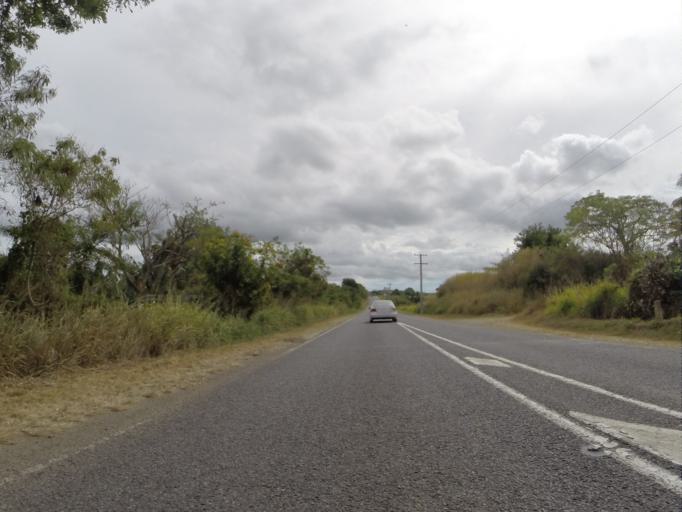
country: FJ
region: Western
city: Nadi
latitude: -18.0402
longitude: 177.3359
